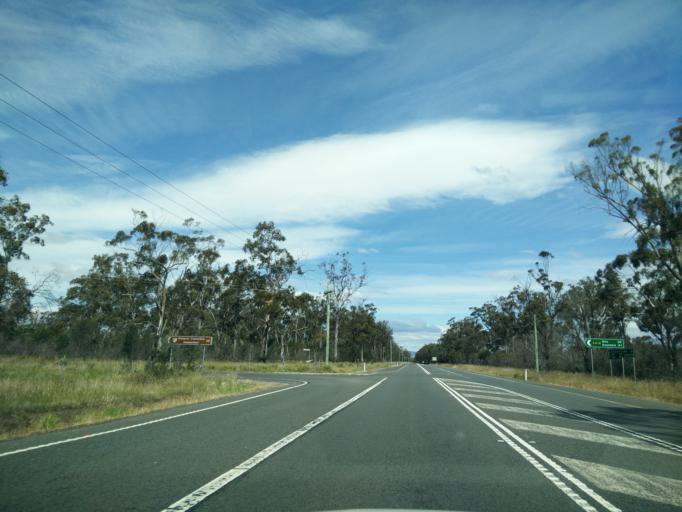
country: AU
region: Tasmania
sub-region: Northern Midlands
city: Evandale
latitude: -41.8195
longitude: 147.4230
